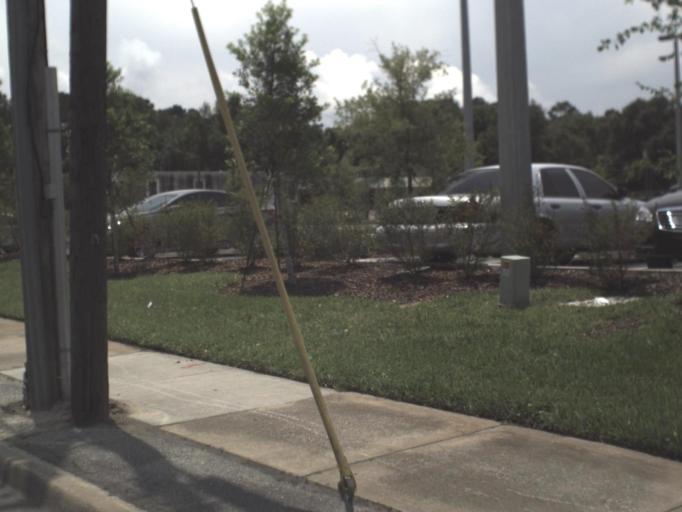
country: US
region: Florida
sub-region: Nassau County
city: Callahan
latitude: 30.5623
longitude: -81.8280
